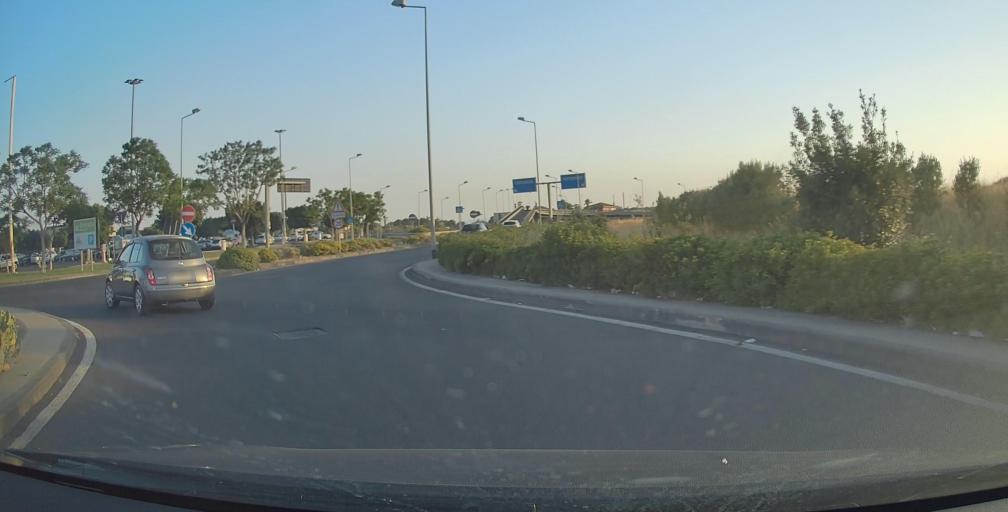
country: IT
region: Sicily
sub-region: Catania
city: Palazzolo
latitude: 37.5482
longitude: 14.9473
